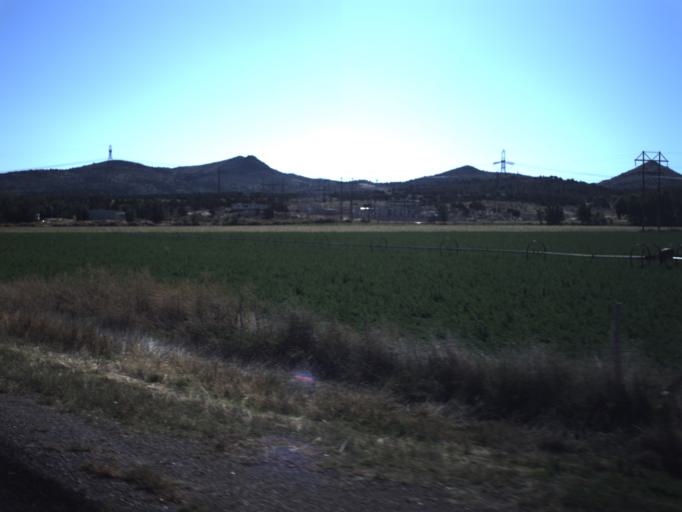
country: US
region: Utah
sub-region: Washington County
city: Enterprise
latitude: 37.6731
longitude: -113.5384
